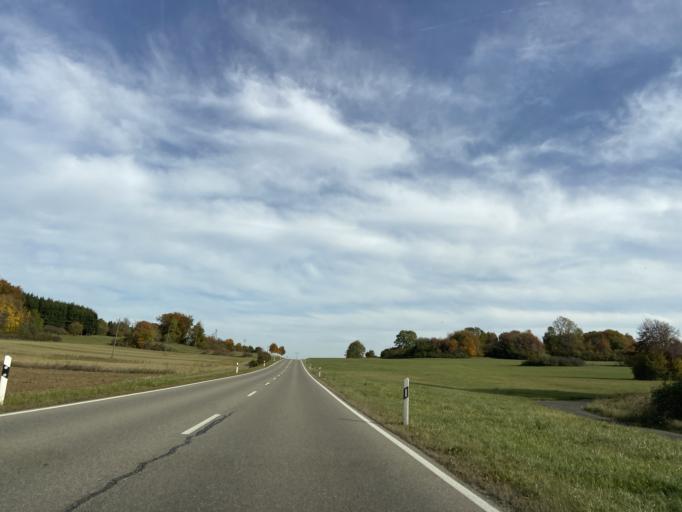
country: DE
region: Baden-Wuerttemberg
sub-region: Tuebingen Region
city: Schwenningen
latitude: 48.1091
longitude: 9.0086
